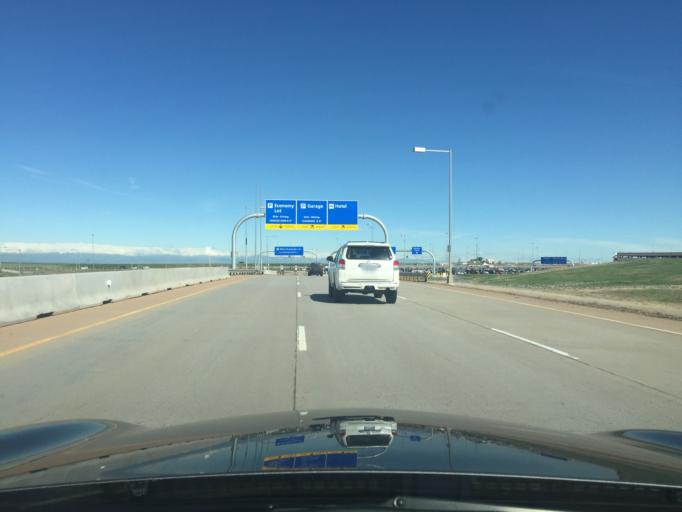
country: US
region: Colorado
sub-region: Weld County
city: Lochbuie
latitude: 39.8430
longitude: -104.6751
